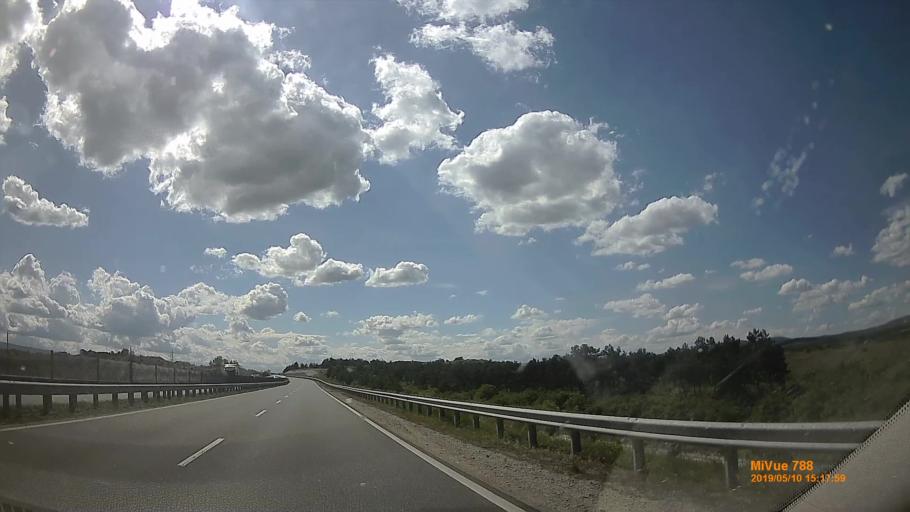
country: HU
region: Veszprem
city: Hajmasker
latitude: 47.1466
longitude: 18.0588
